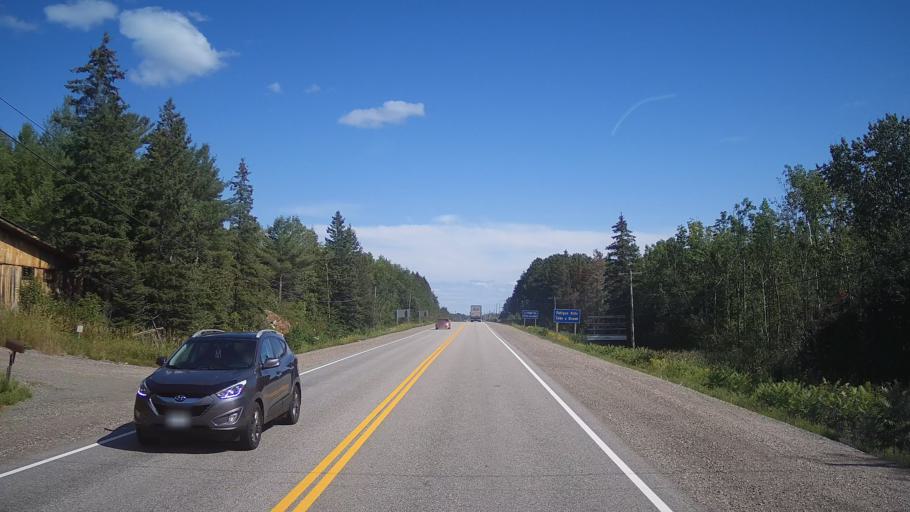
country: CA
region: Ontario
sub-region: Nipissing District
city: North Bay
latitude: 46.3834
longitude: -79.9852
